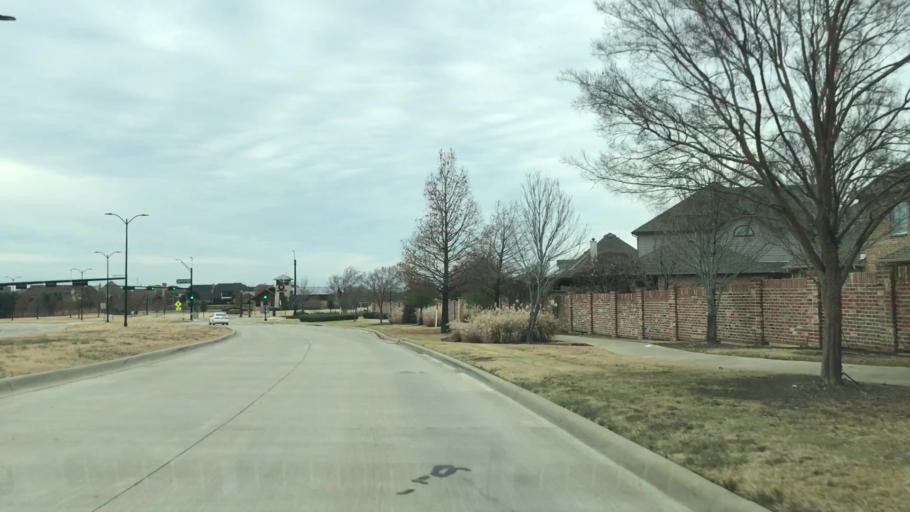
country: US
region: Texas
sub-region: Denton County
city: The Colony
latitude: 33.1275
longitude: -96.8931
